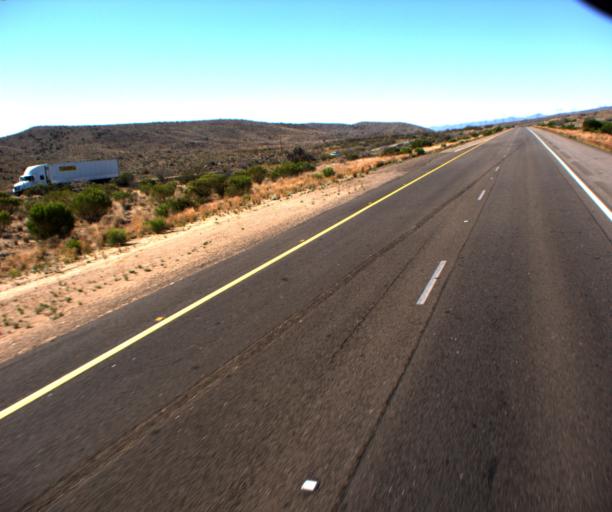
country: US
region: Arizona
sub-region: Mohave County
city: Kingman
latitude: 34.9827
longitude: -113.6683
